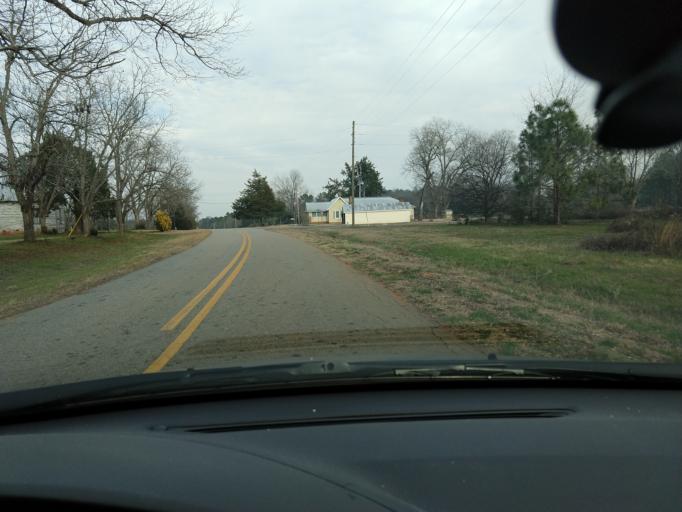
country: US
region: Georgia
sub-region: Webster County
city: Preston
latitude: 32.0268
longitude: -84.4248
